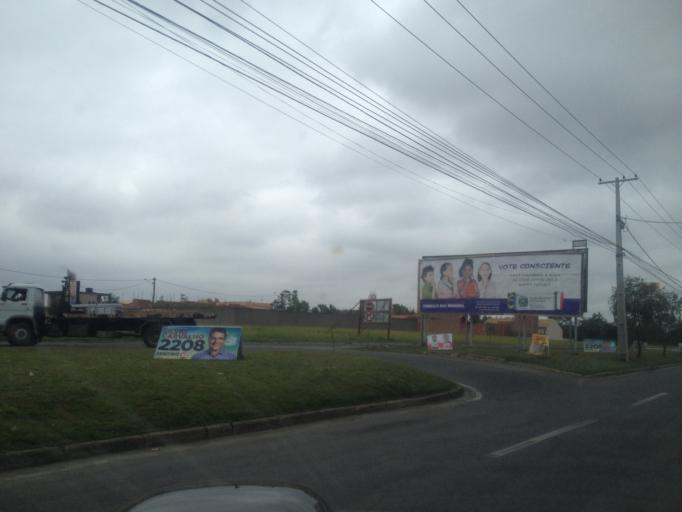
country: BR
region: Rio de Janeiro
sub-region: Porto Real
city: Porto Real
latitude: -22.4141
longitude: -44.3106
